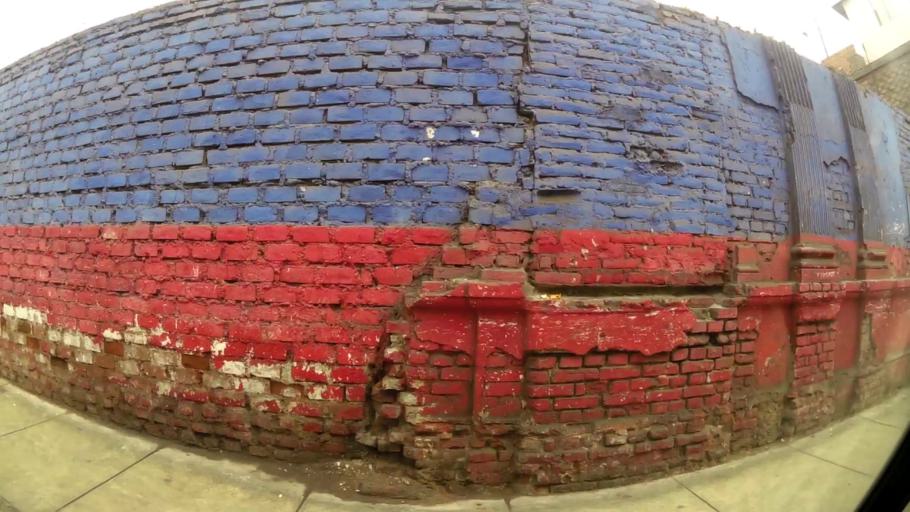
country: PE
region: Lima
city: Lima
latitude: -12.0455
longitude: -77.0396
